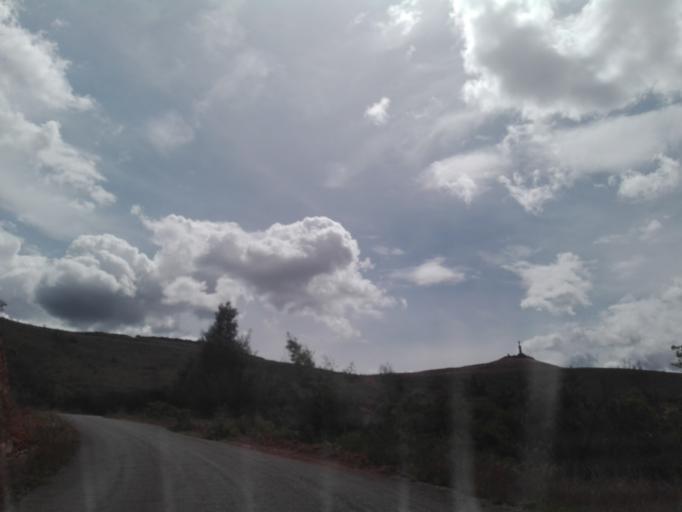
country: CO
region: Boyaca
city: Raquira
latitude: 5.5408
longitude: -73.6176
